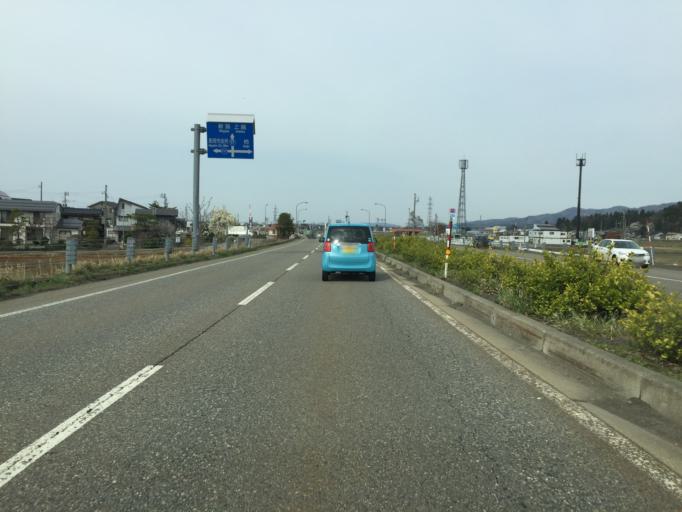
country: JP
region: Niigata
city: Nagaoka
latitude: 37.4241
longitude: 138.8624
